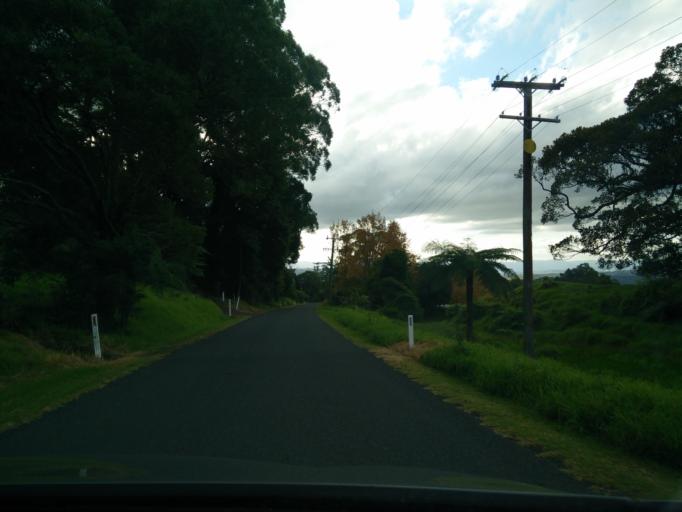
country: AU
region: New South Wales
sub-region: Kiama
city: Jamberoo
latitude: -34.6918
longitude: 150.7879
